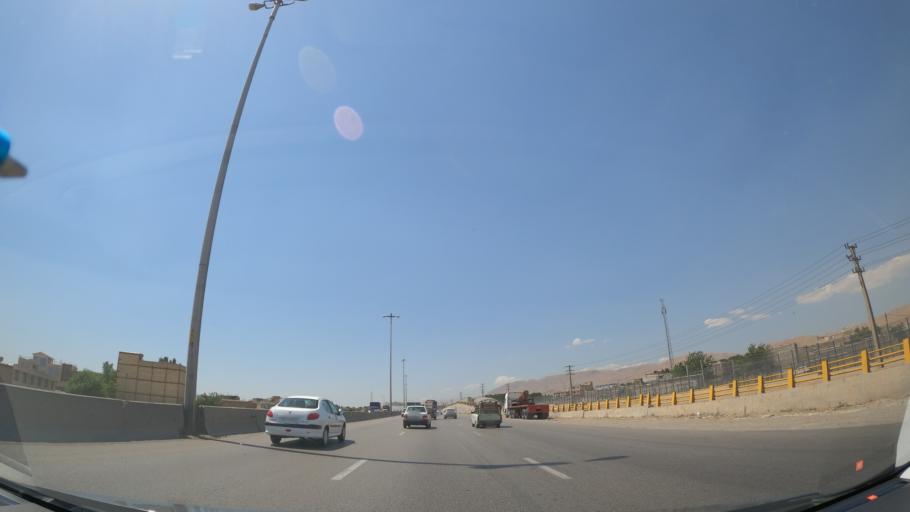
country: IR
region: Alborz
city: Karaj
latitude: 35.8647
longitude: 50.9034
